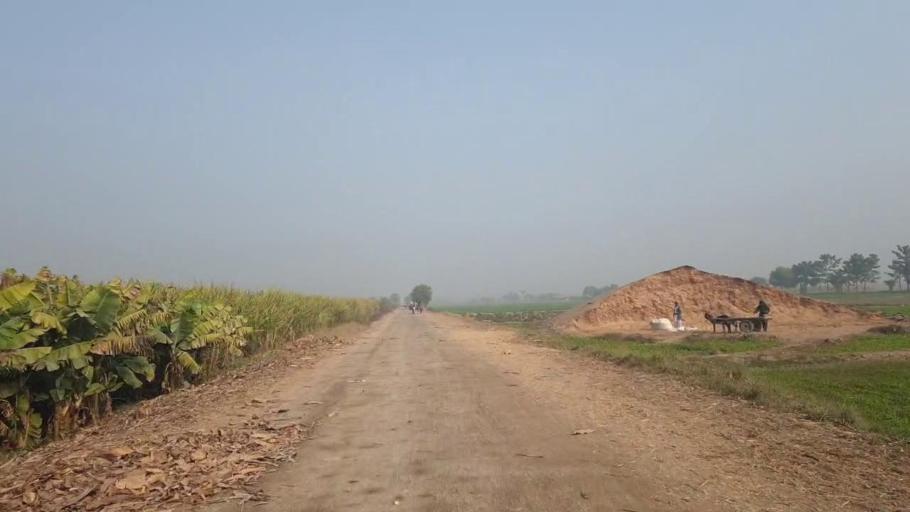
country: PK
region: Sindh
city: Tando Adam
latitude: 25.8119
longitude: 68.6153
